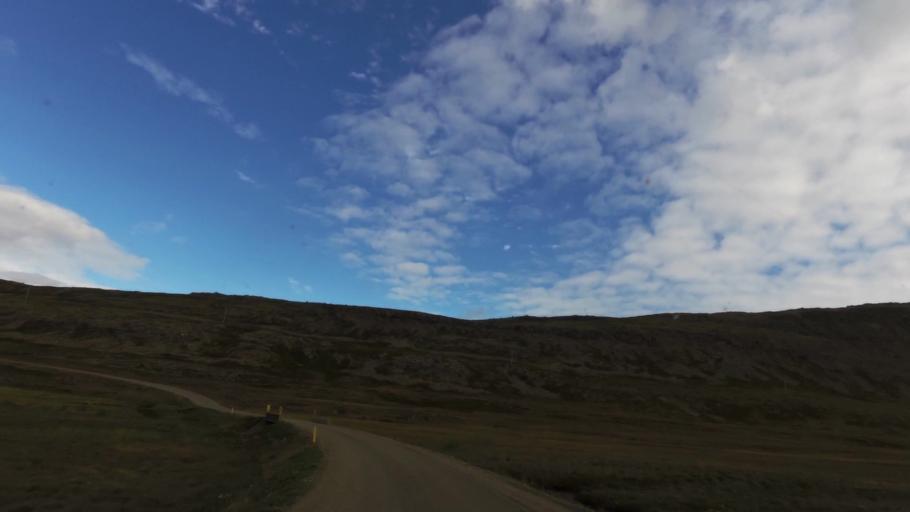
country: IS
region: West
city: Olafsvik
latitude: 65.5595
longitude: -24.1762
